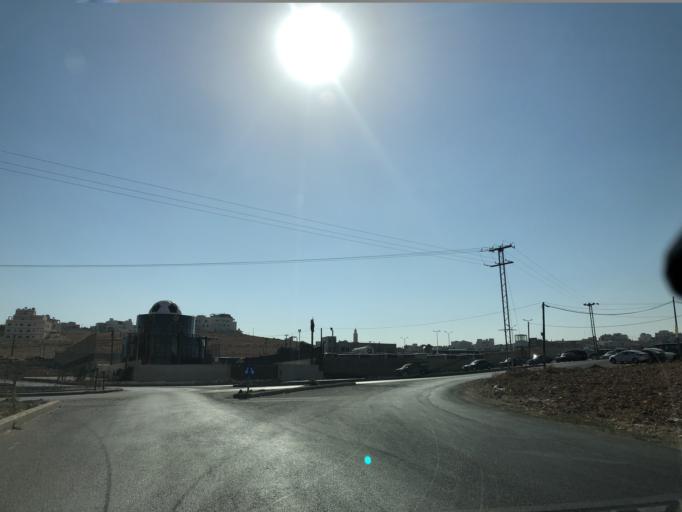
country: JO
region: Amman
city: Wadi as Sir
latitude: 31.9341
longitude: 35.8448
